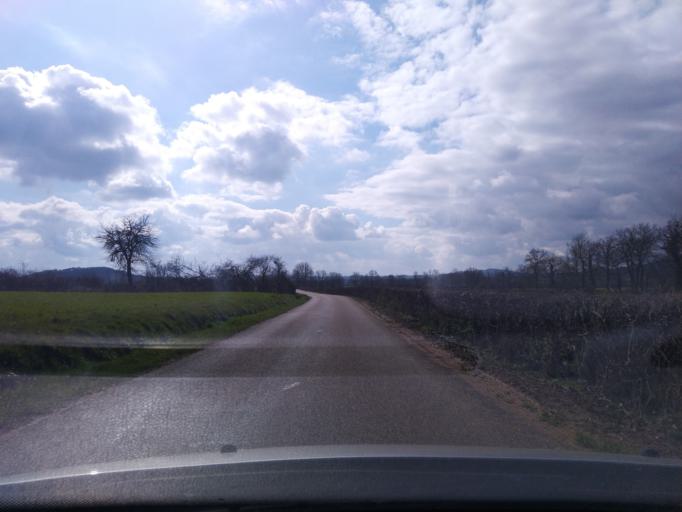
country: FR
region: Bourgogne
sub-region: Departement de l'Yonne
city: Avallon
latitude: 47.5536
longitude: 4.0567
